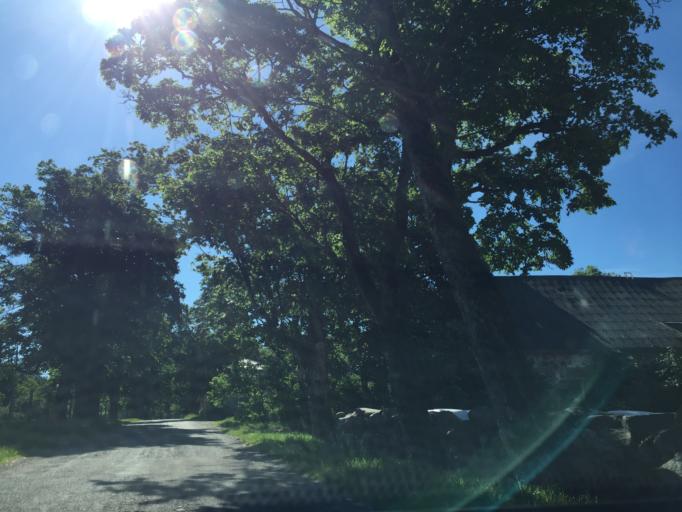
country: LV
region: Ventspils Rajons
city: Piltene
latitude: 57.3278
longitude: 22.0136
